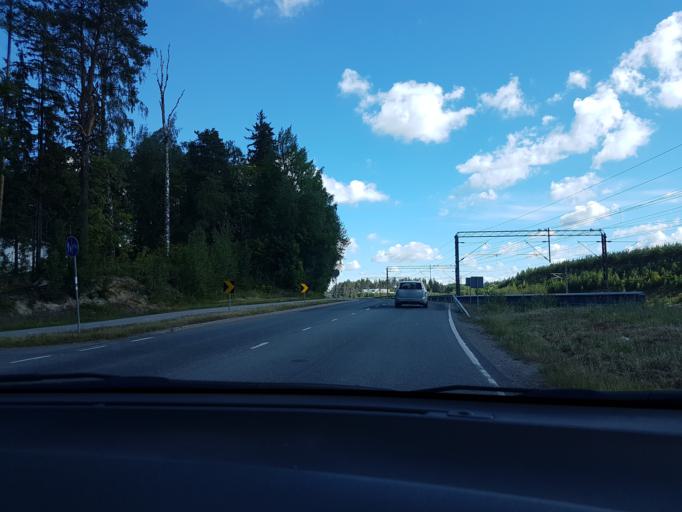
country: FI
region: Uusimaa
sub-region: Helsinki
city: Kerava
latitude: 60.3727
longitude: 25.0940
